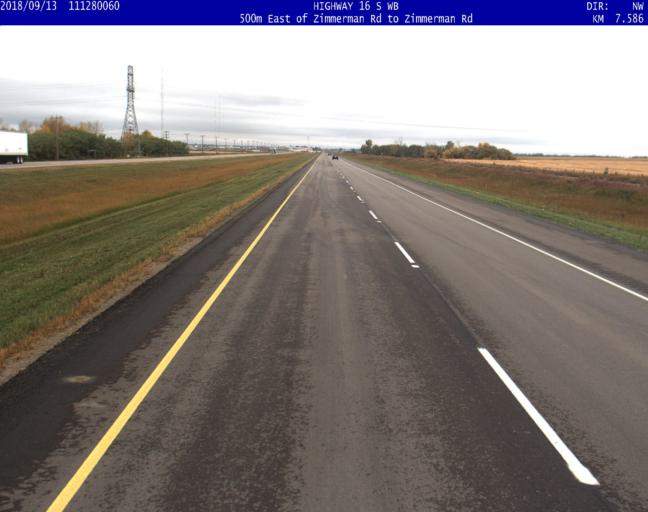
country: CA
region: Saskatchewan
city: Saskatoon
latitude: 52.0714
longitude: -106.4978
